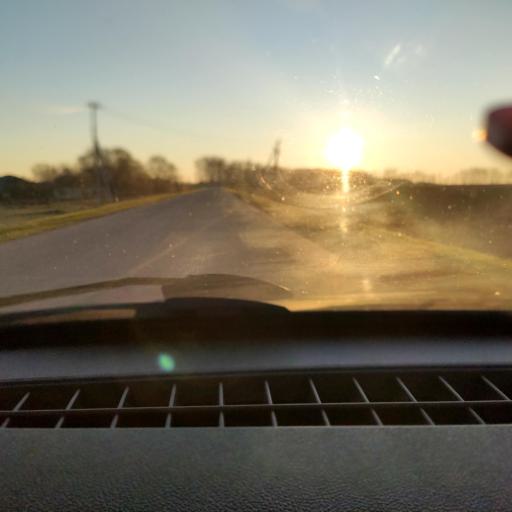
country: RU
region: Bashkortostan
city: Avdon
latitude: 54.5511
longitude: 55.6617
